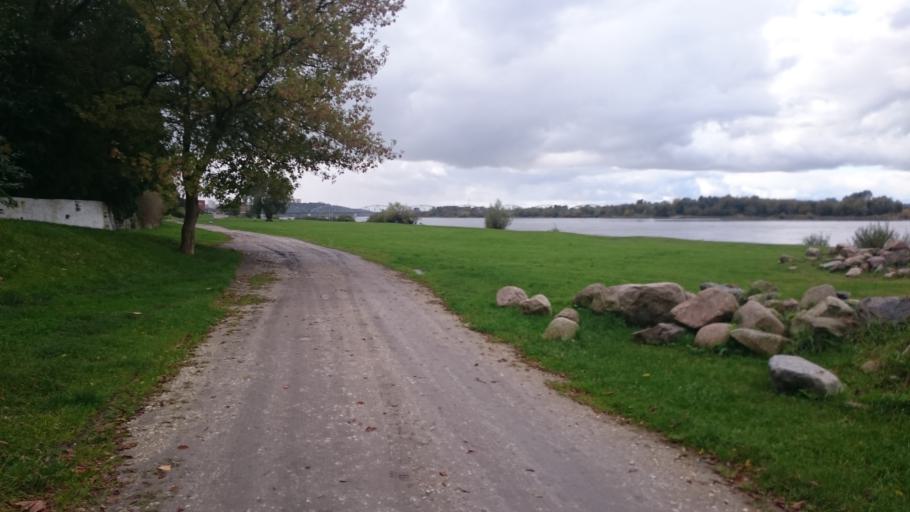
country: PL
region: Kujawsko-Pomorskie
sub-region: Grudziadz
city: Grudziadz
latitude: 53.4964
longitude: 18.7485
